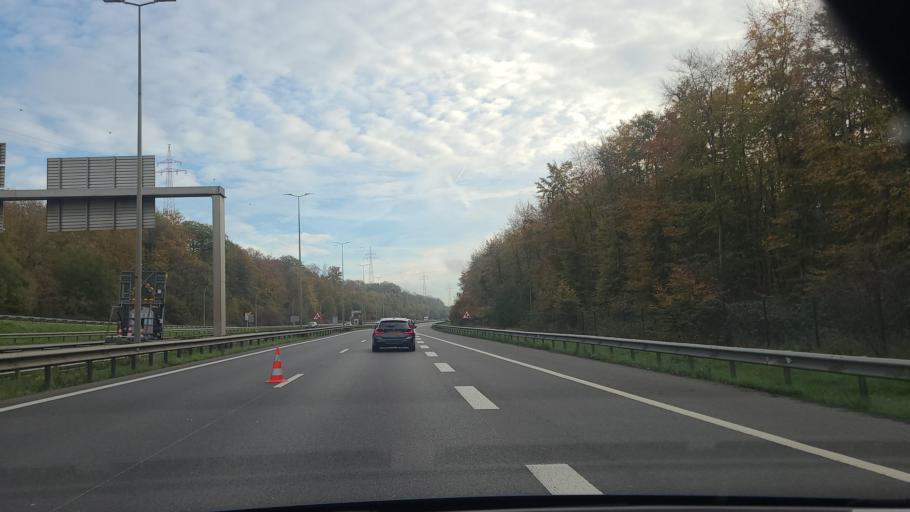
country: LU
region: Luxembourg
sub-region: Canton de Luxembourg
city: Sandweiler
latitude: 49.6406
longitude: 6.1931
